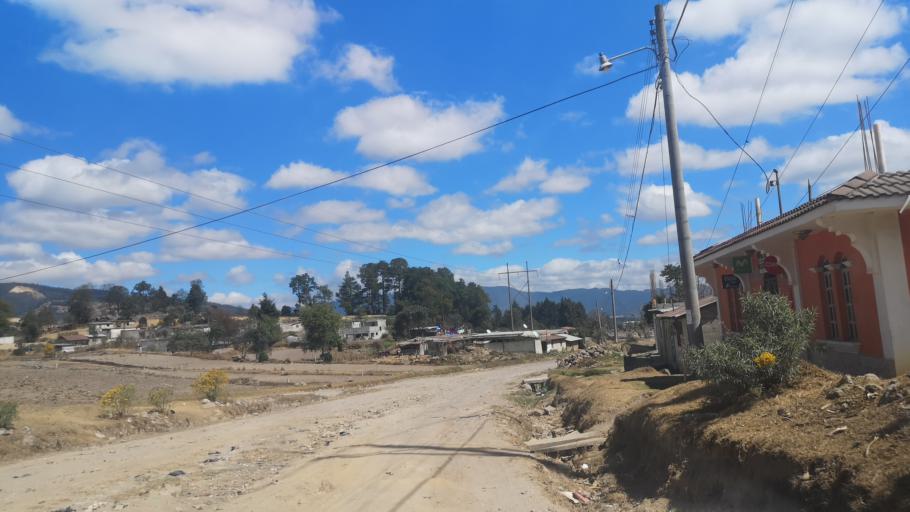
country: GT
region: Quetzaltenango
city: Almolonga
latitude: 14.7956
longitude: -91.5374
